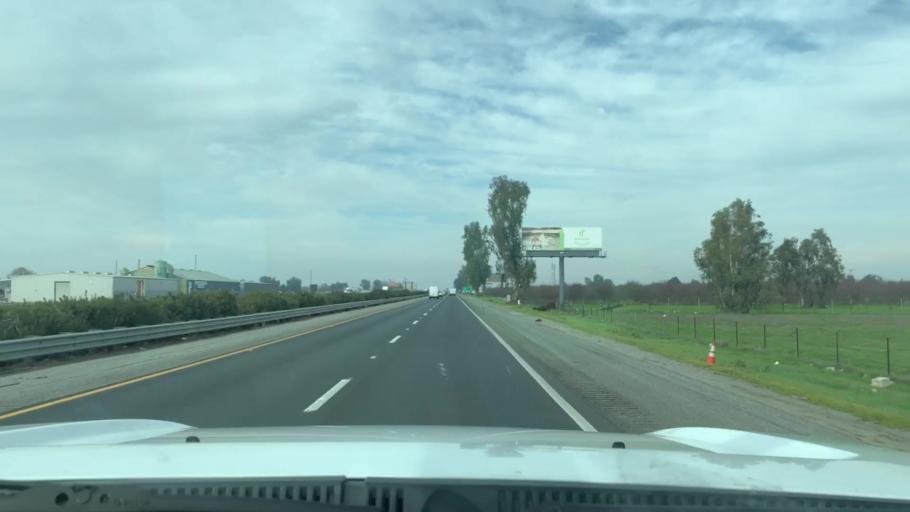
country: US
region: California
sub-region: Tulare County
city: Pixley
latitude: 35.9811
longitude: -119.2963
